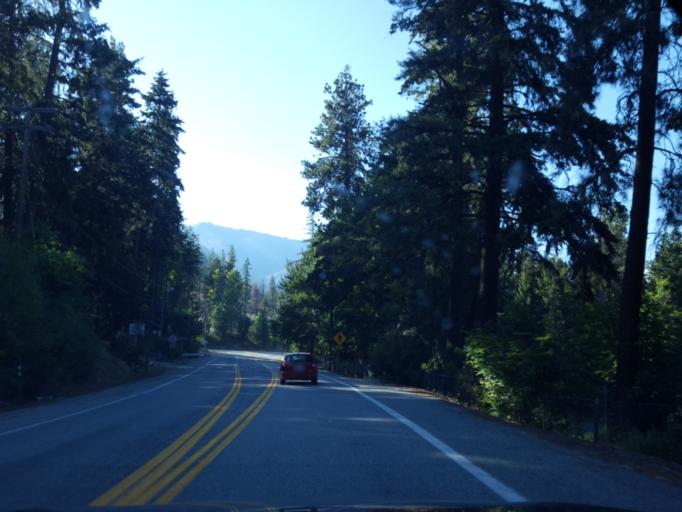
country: US
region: Washington
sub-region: Chelan County
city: Granite Falls
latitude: 47.8729
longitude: -120.1993
